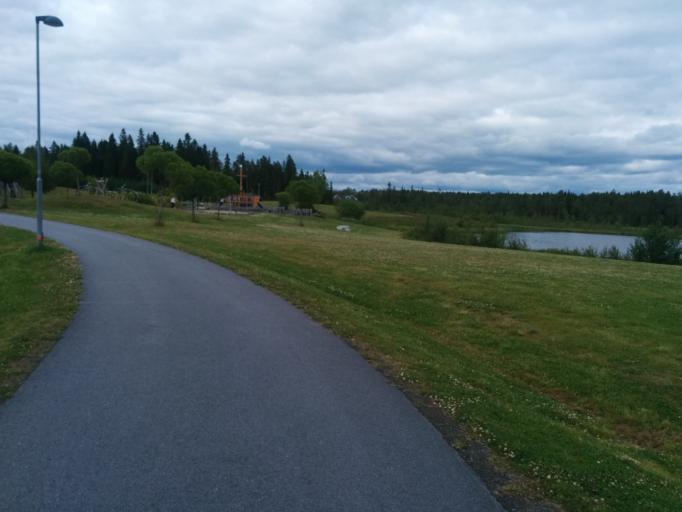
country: SE
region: Vaesterbotten
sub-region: Umea Kommun
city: Holmsund
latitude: 63.8030
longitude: 20.3746
